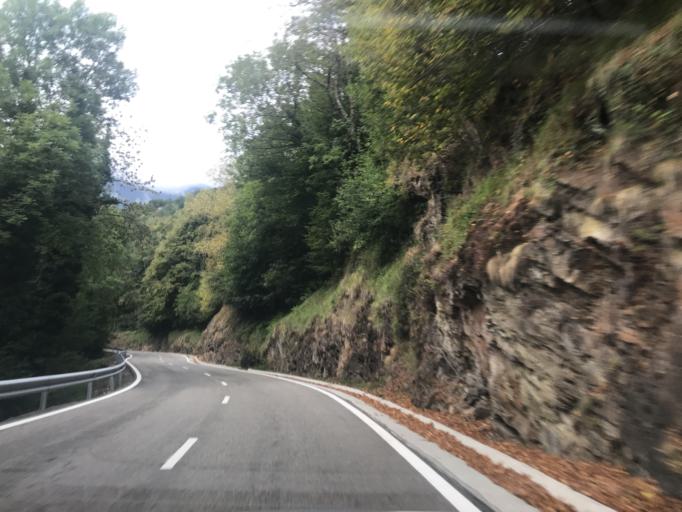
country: ES
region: Catalonia
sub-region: Provincia de Lleida
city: Les
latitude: 42.7766
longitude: 0.6819
